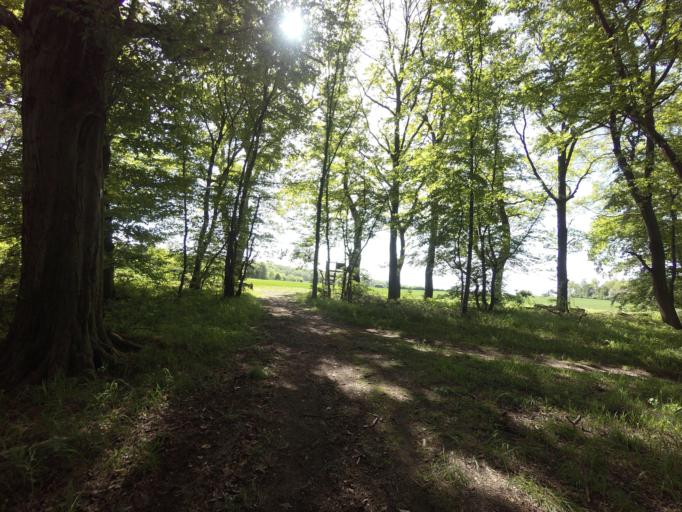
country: DE
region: Lower Saxony
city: Cremlingen
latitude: 52.2927
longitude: 10.6293
